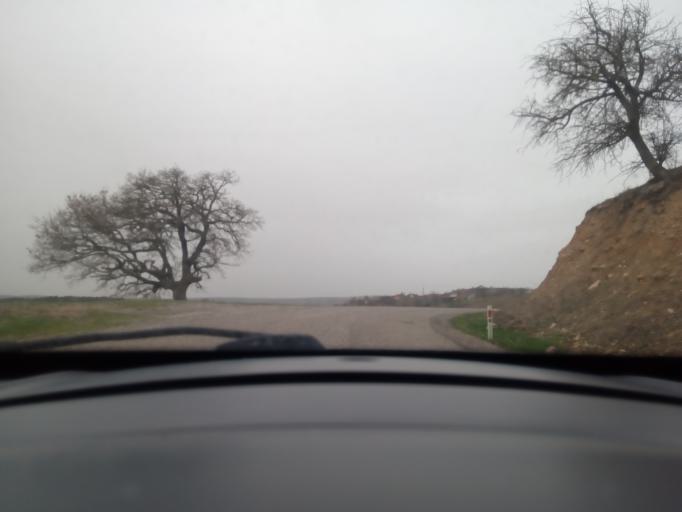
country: TR
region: Balikesir
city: Susurluk
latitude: 39.9150
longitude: 28.0978
